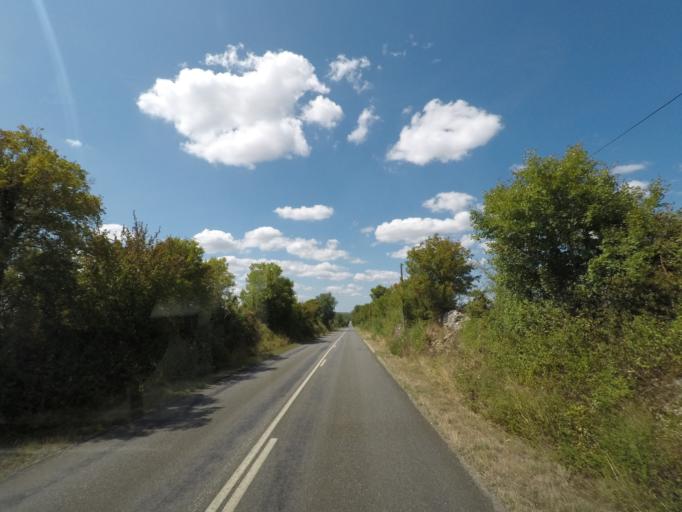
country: FR
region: Midi-Pyrenees
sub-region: Departement du Lot
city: Lacapelle-Marival
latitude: 44.6258
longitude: 1.8484
